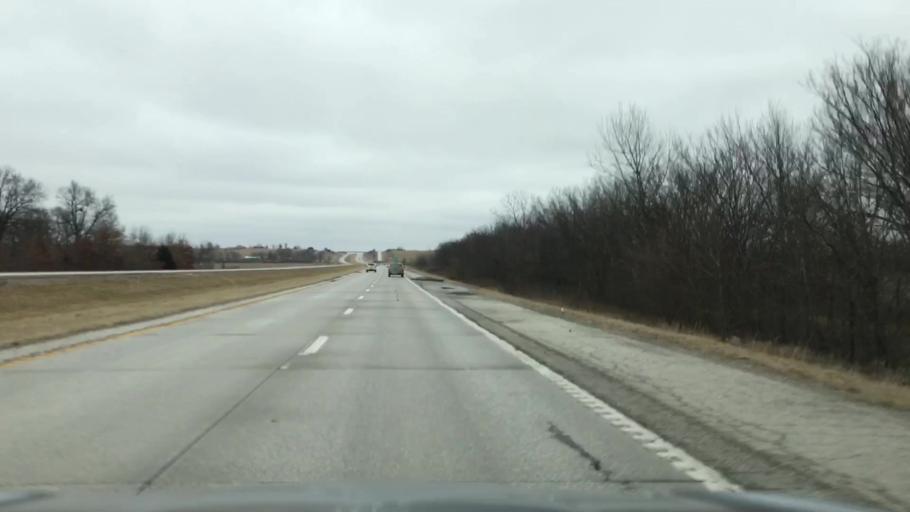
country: US
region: Missouri
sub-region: Linn County
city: Marceline
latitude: 39.7611
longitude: -92.9744
